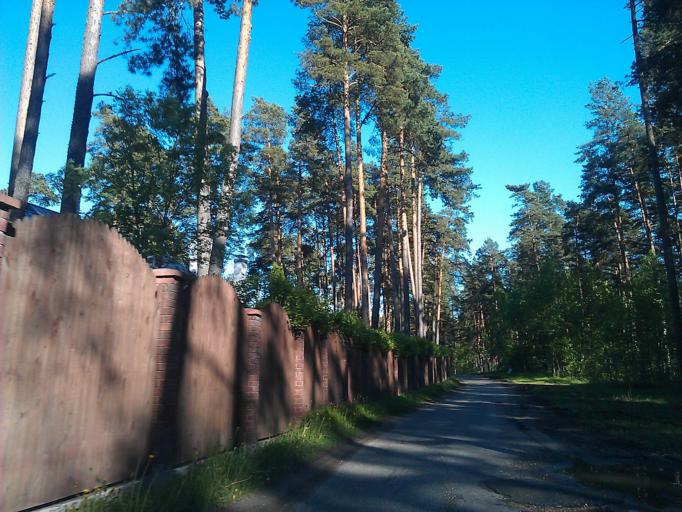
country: LV
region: Riga
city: Bergi
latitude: 57.0138
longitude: 24.2774
